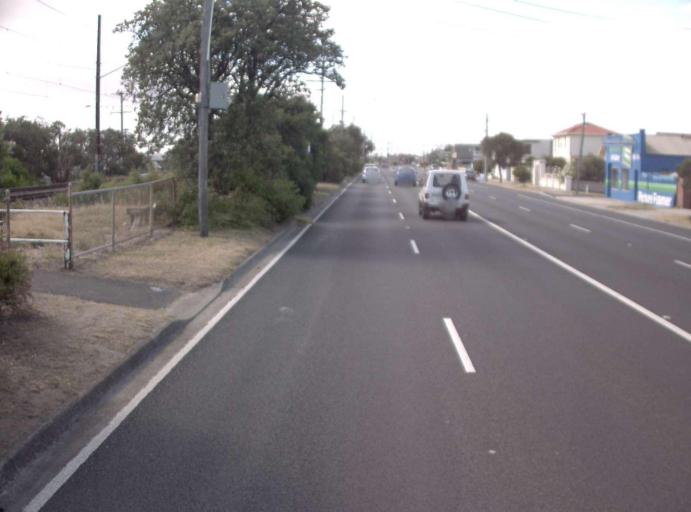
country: AU
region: Victoria
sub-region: Kingston
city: Aspendale
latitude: -38.0219
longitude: 145.0984
